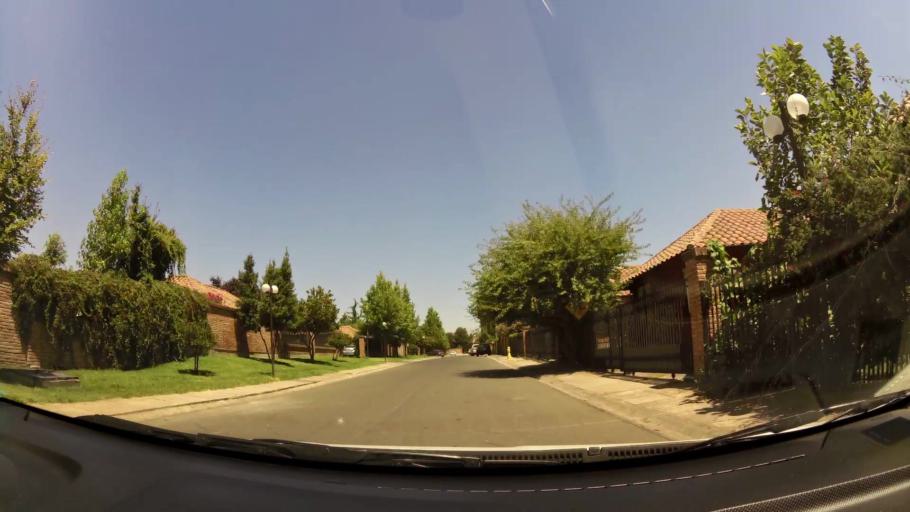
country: CL
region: Maule
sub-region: Provincia de Talca
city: Talca
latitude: -35.4324
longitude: -71.6260
